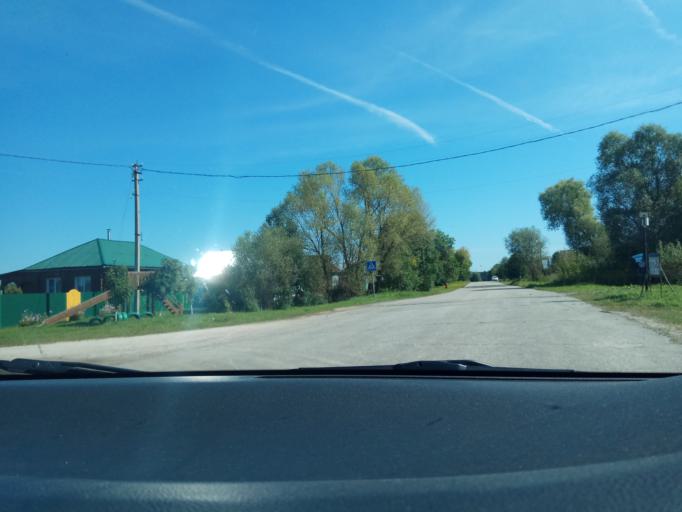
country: RU
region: Vladimir
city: Dobryatino
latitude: 55.7344
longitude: 41.4353
